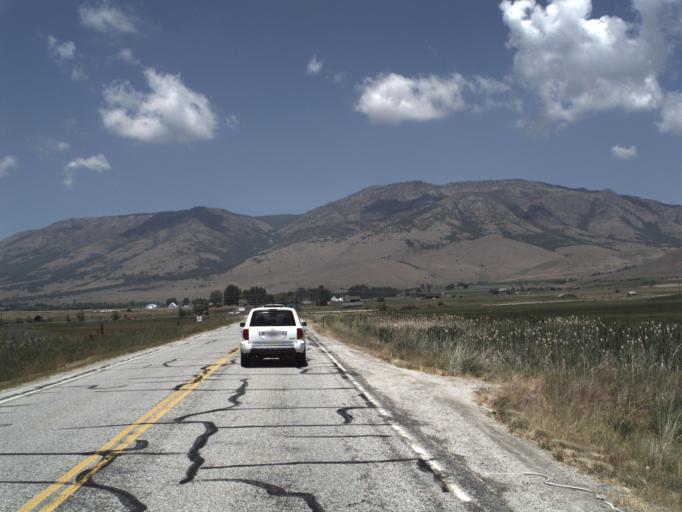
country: US
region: Utah
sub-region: Weber County
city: Wolf Creek
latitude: 41.2557
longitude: -111.7612
